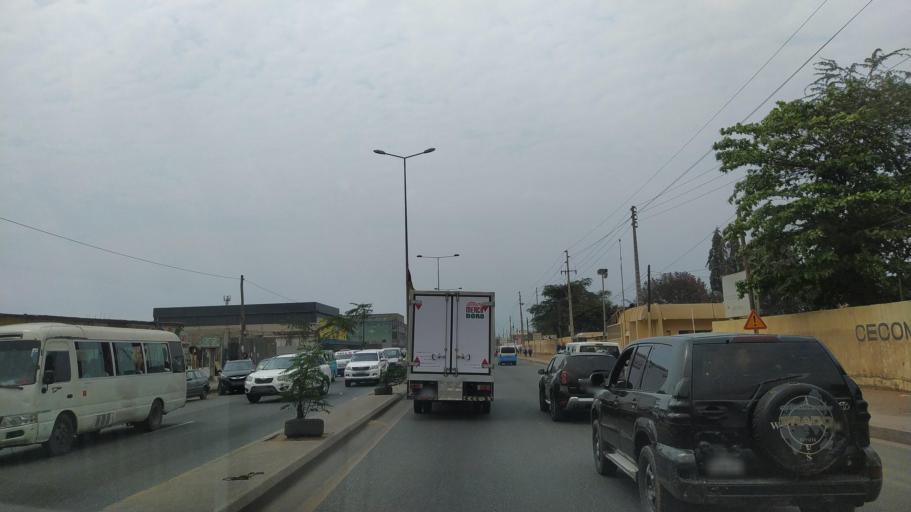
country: AO
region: Luanda
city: Luanda
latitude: -8.8644
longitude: 13.2816
